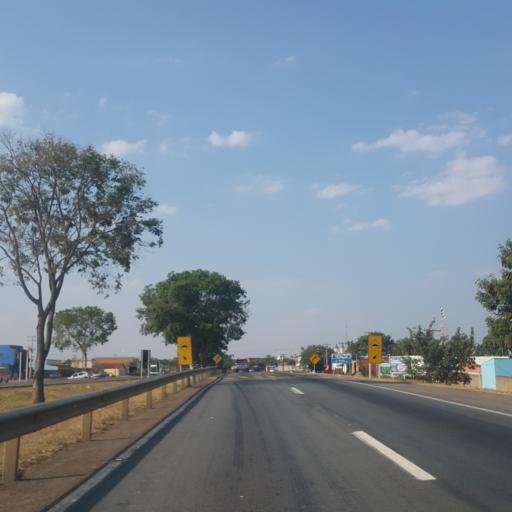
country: BR
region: Goias
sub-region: Abadiania
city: Abadiania
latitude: -16.0920
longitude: -48.5144
